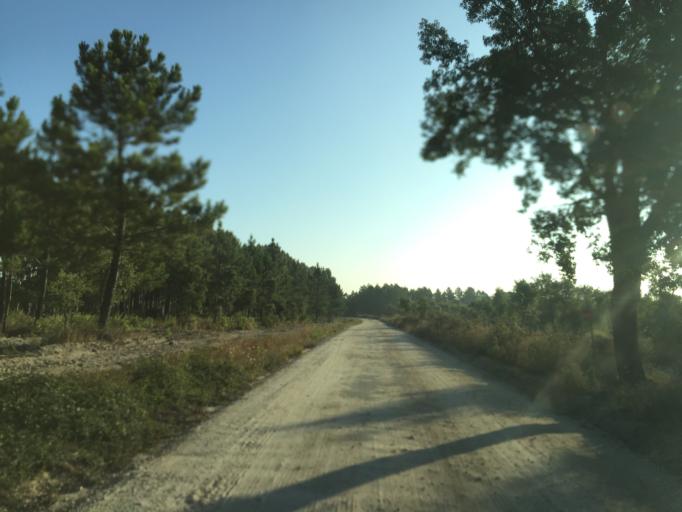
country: PT
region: Portalegre
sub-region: Ponte de Sor
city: Santo Andre
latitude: 39.1272
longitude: -8.3214
